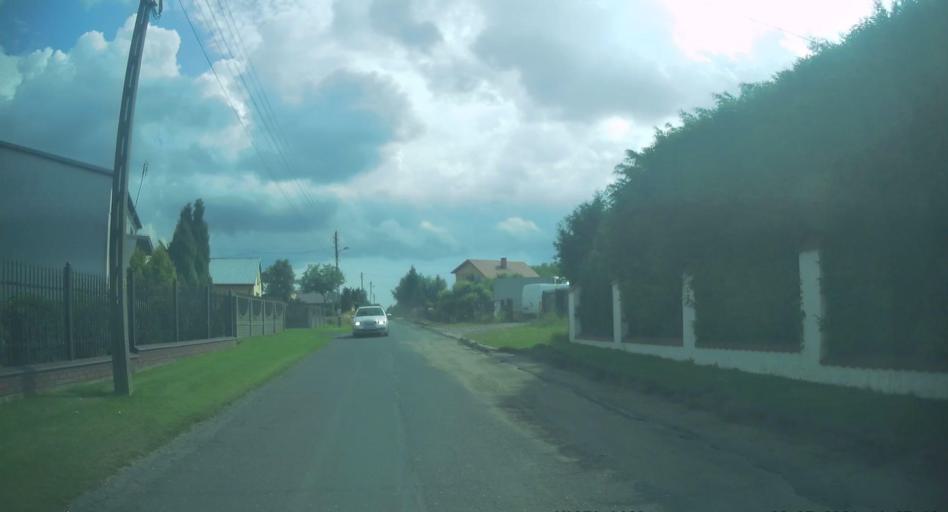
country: PL
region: Lodz Voivodeship
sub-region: Powiat brzezinski
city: Rogow
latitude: 51.8129
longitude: 19.8964
